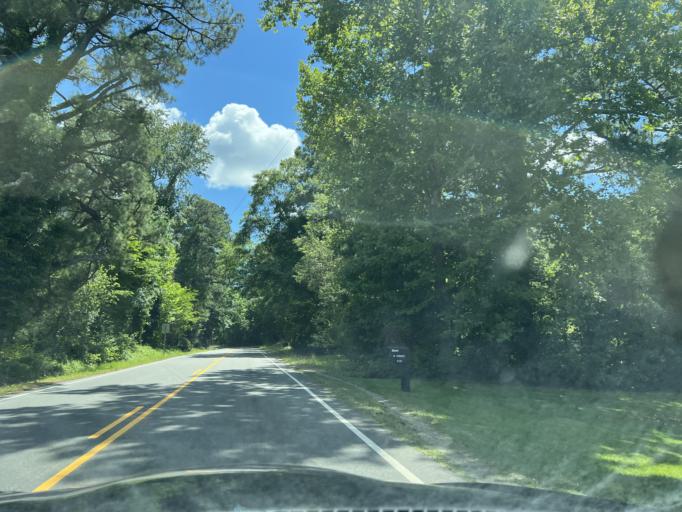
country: US
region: North Carolina
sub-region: Lee County
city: Sanford
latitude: 35.4559
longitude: -79.1680
